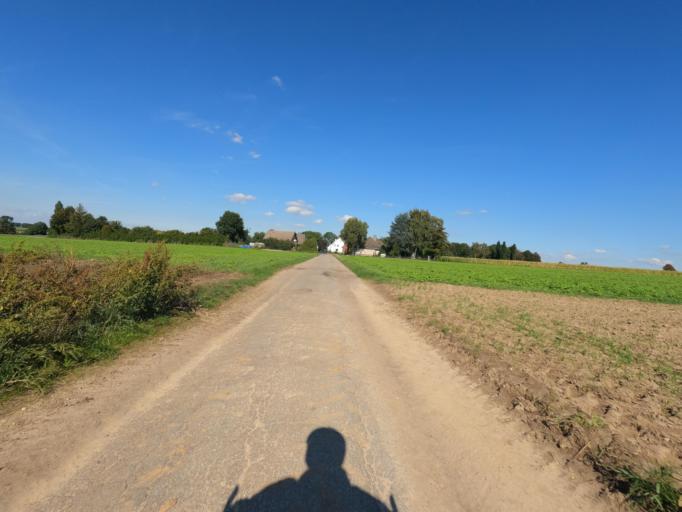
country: DE
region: North Rhine-Westphalia
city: Siersdorf
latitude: 50.8914
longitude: 6.2176
